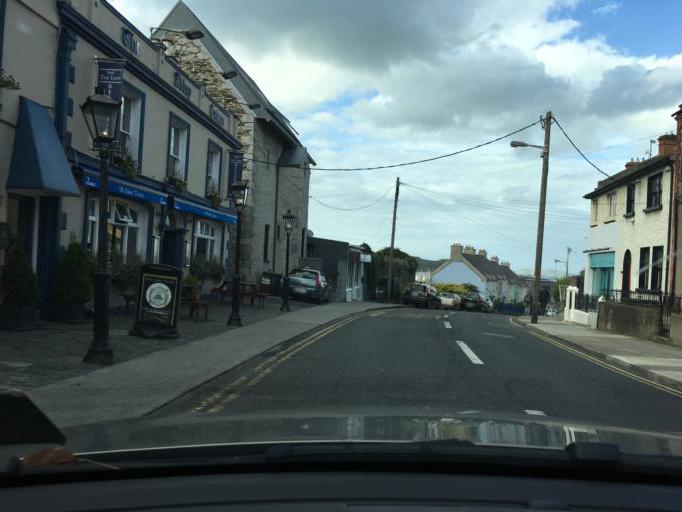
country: IE
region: Leinster
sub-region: Fingal County
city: Howth
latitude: 53.3869
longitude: -6.0656
